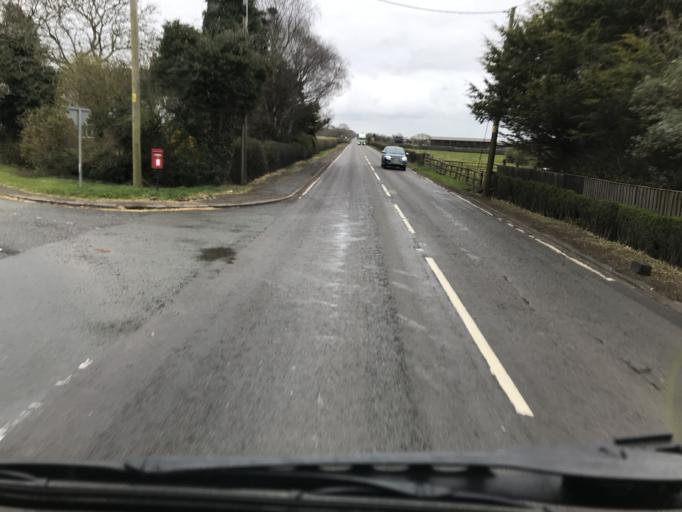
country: GB
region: England
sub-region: Cheshire West and Chester
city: Tattenhall
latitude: 53.0951
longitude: -2.7764
